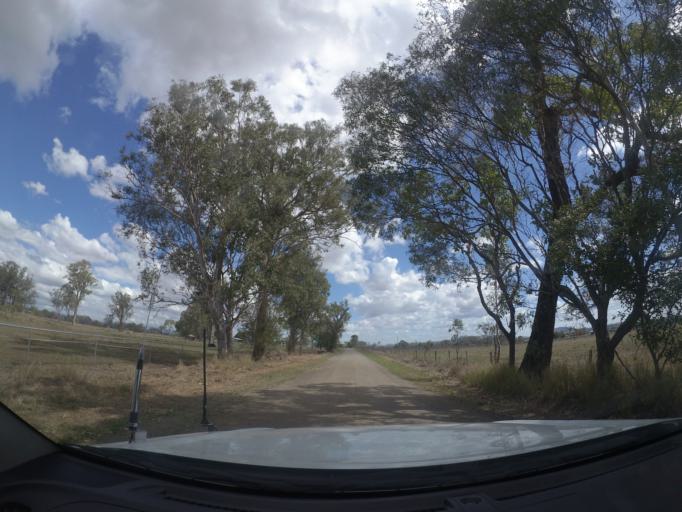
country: AU
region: Queensland
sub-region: Logan
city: Cedar Vale
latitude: -27.8945
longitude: 152.9588
